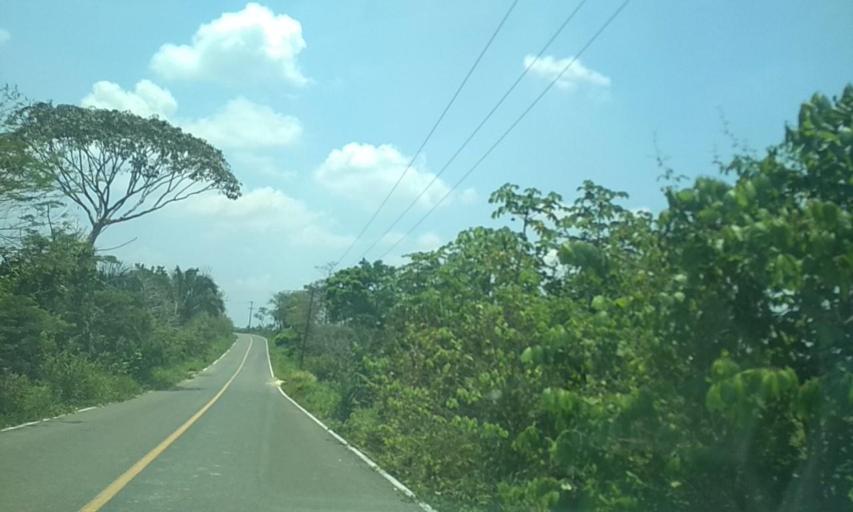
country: MX
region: Tabasco
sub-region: Huimanguillo
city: Francisco Rueda
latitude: 17.7604
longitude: -94.0573
